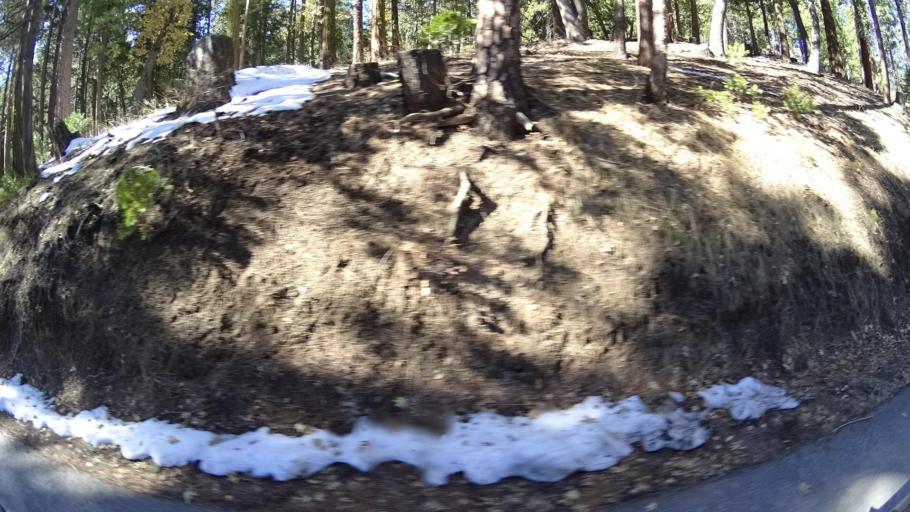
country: US
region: California
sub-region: Kern County
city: Alta Sierra
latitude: 35.7339
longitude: -118.5535
